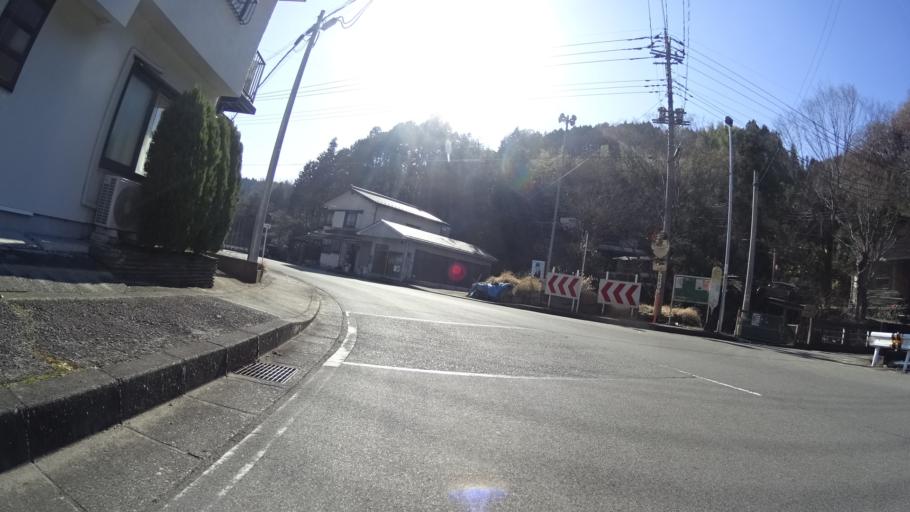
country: JP
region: Yamanashi
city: Uenohara
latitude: 35.6339
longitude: 139.1413
